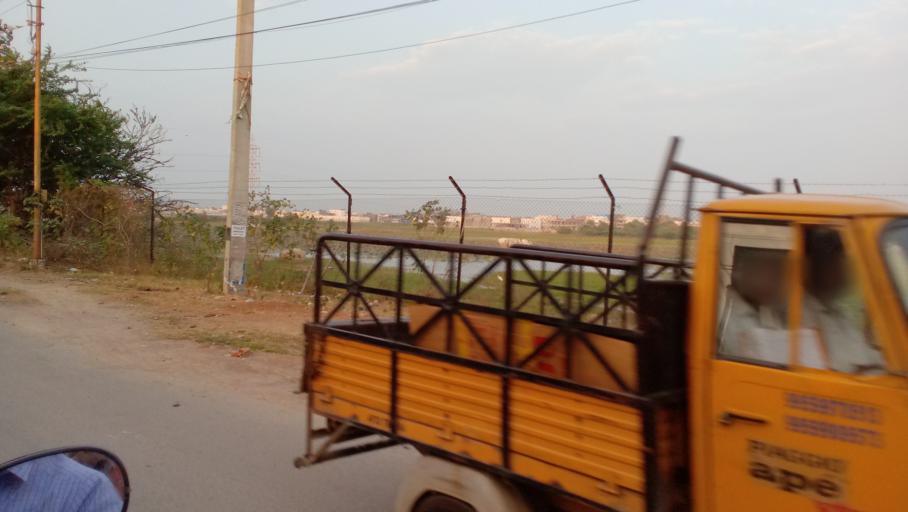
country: IN
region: Telangana
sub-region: Medak
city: Serilingampalle
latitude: 17.5117
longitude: 78.3181
